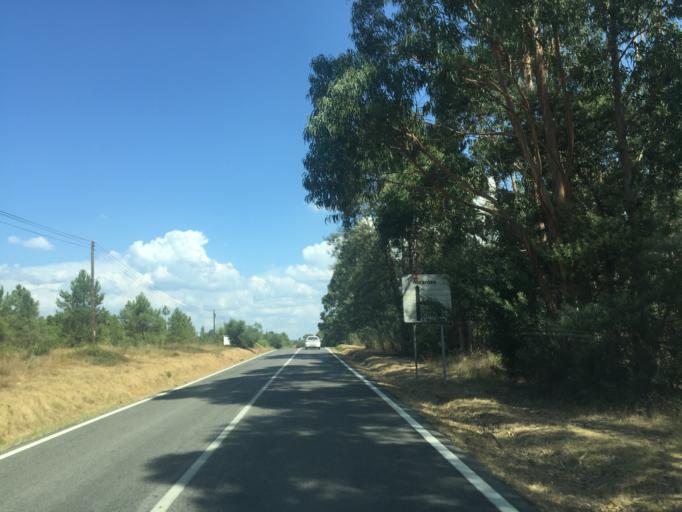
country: PT
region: Santarem
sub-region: Chamusca
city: Vila Nova da Barquinha
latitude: 39.4661
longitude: -8.3893
